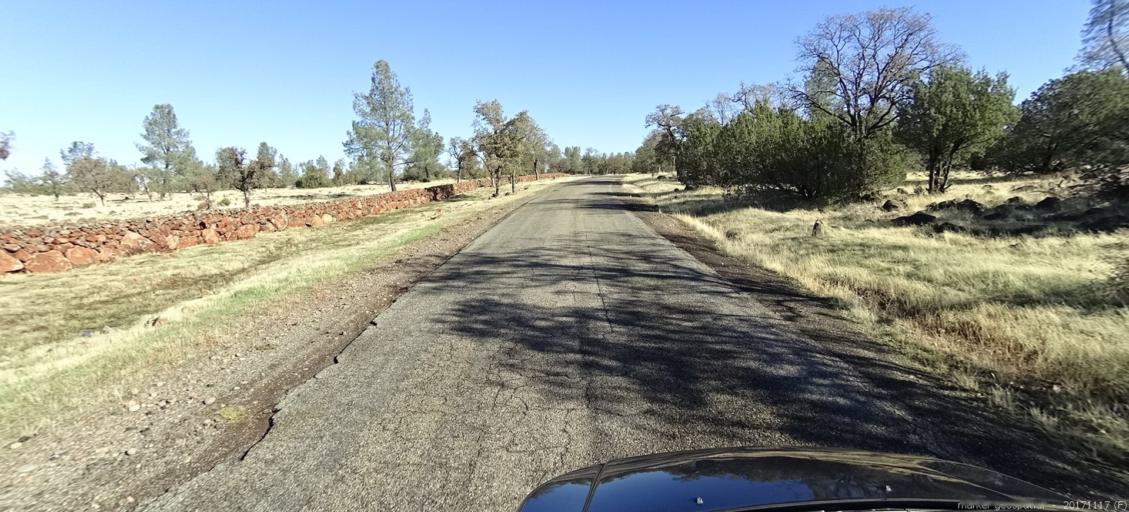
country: US
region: California
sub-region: Shasta County
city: Cottonwood
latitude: 40.4413
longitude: -122.1187
